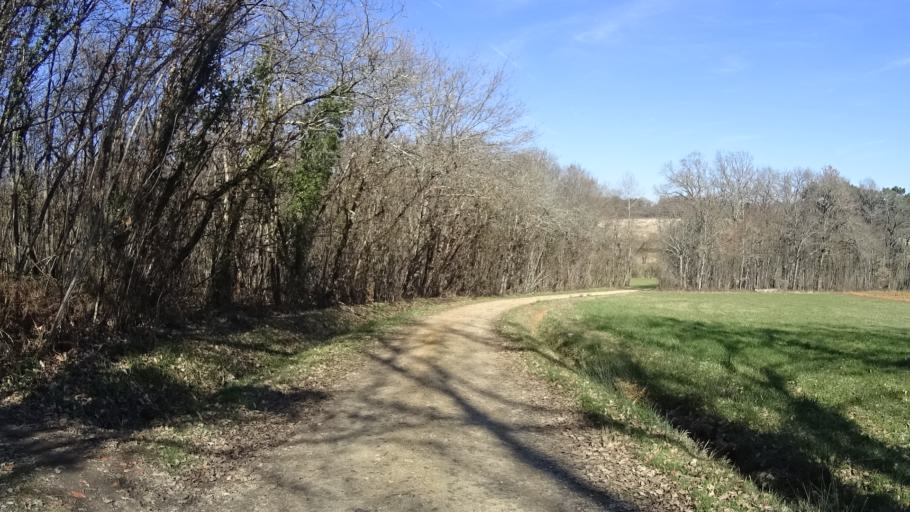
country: FR
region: Aquitaine
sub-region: Departement de la Dordogne
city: Riberac
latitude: 45.2072
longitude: 0.3224
